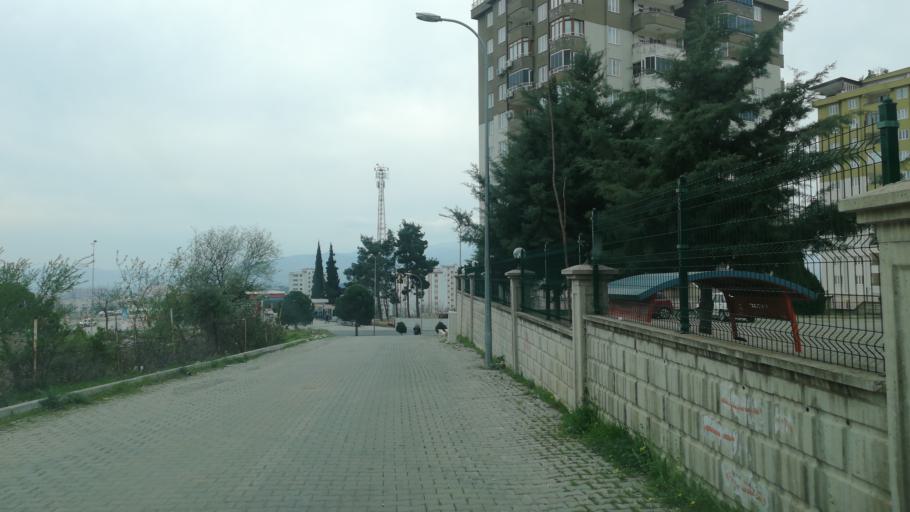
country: TR
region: Kahramanmaras
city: Kahramanmaras
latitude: 37.6010
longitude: 36.8264
